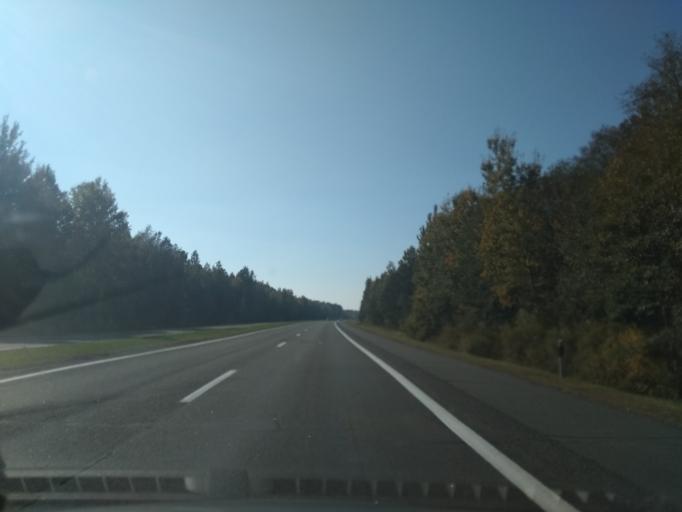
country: BY
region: Brest
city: Ivatsevichy
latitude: 52.7722
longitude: 25.5405
